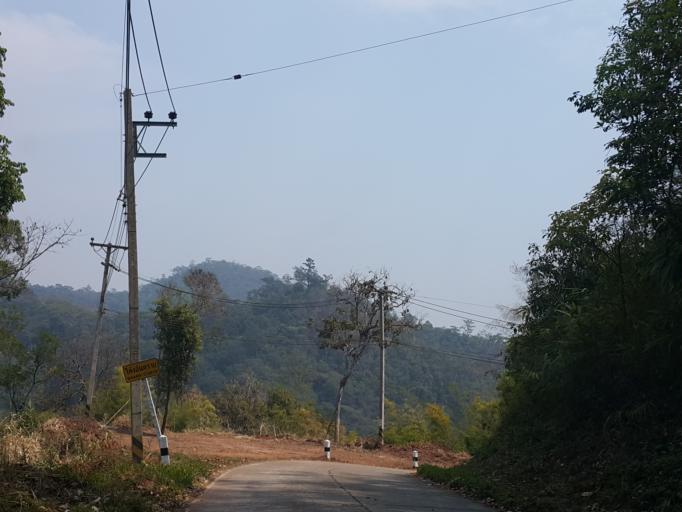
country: TH
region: Lampang
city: Mueang Pan
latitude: 18.8223
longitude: 99.4281
